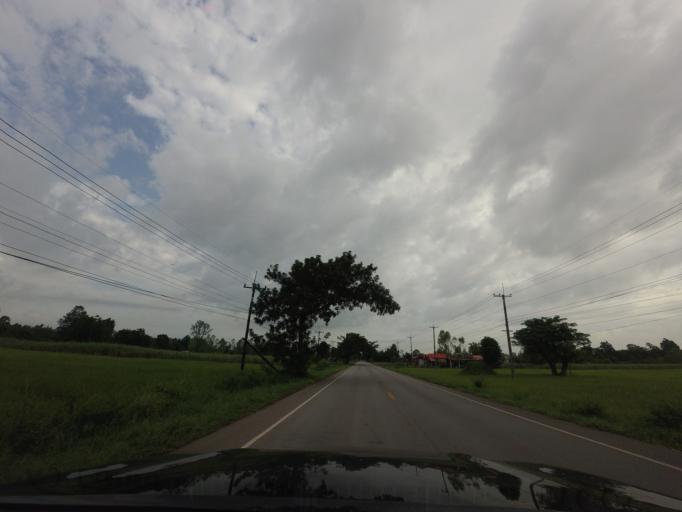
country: TH
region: Changwat Udon Thani
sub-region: Amphoe Ban Phue
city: Ban Phue
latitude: 17.7313
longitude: 102.3958
